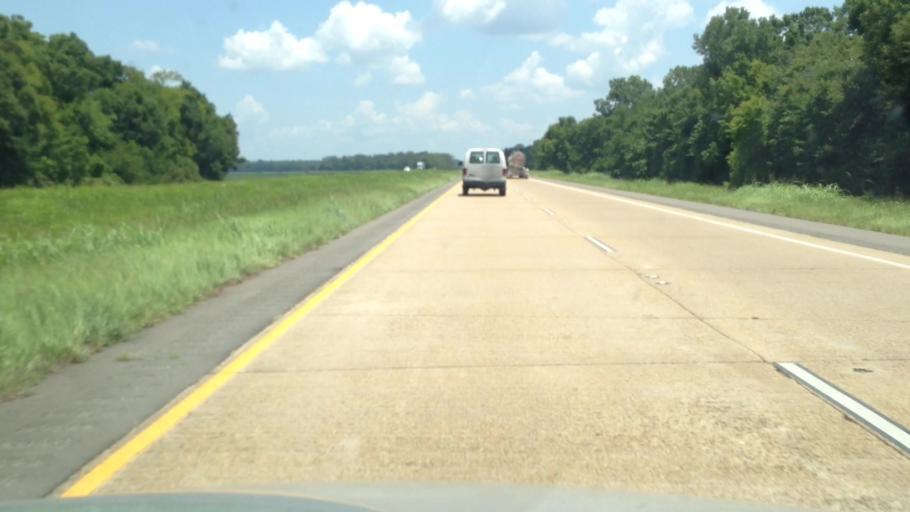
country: US
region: Louisiana
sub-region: Rapides Parish
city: Lecompte
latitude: 31.0060
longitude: -92.3547
